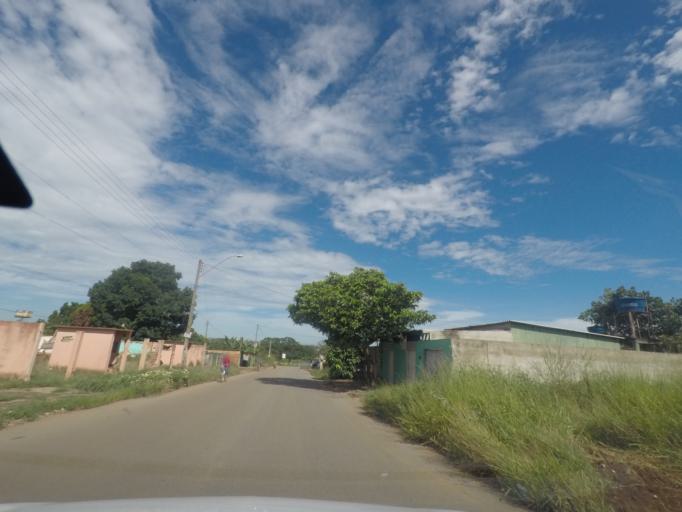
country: BR
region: Goias
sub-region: Aparecida De Goiania
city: Aparecida de Goiania
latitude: -16.8118
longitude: -49.2919
